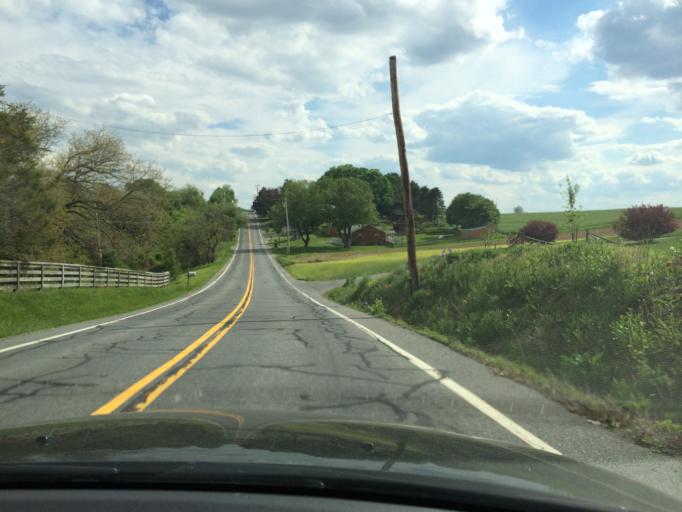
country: US
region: Maryland
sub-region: Carroll County
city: Westminster
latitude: 39.5121
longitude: -77.0019
